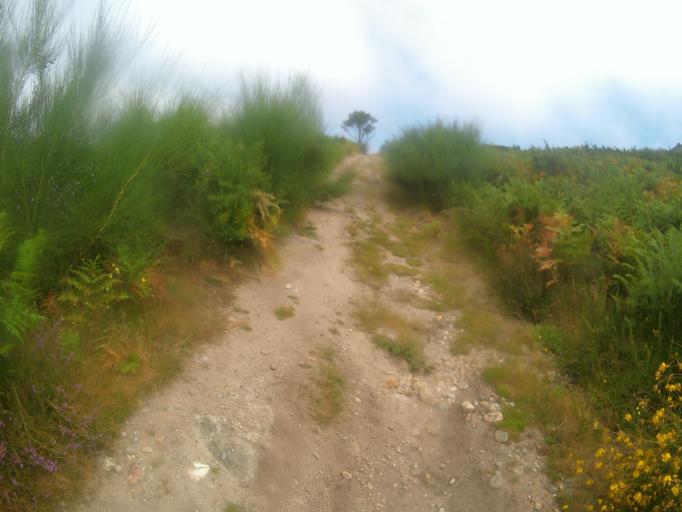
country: PT
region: Viana do Castelo
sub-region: Ponte de Lima
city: Ponte de Lima
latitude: 41.7211
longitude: -8.6016
